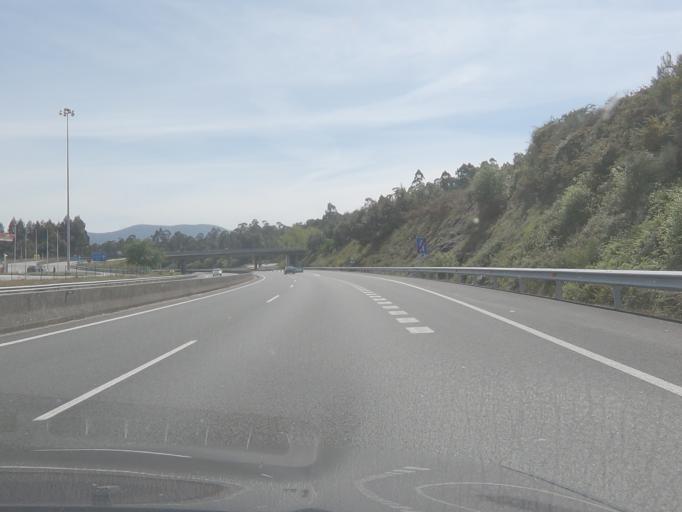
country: ES
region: Galicia
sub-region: Provincia de Pontevedra
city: Portas
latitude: 42.5637
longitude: -8.6723
